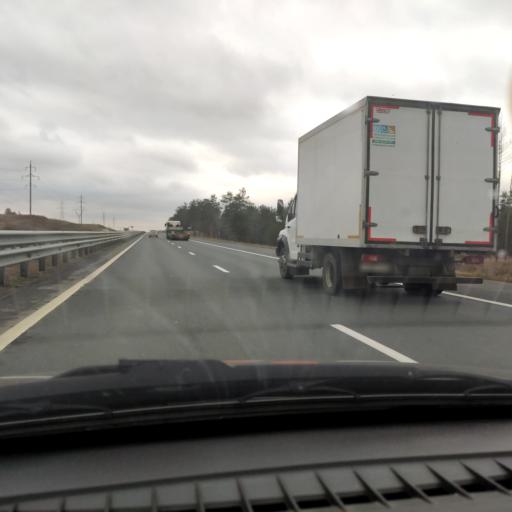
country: RU
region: Samara
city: Povolzhskiy
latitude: 53.5149
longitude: 49.6512
